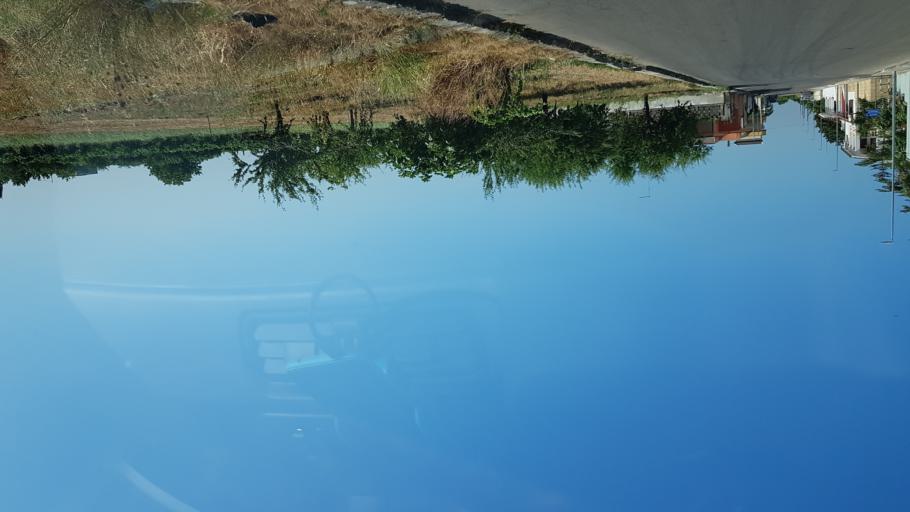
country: IT
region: Apulia
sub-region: Provincia di Brindisi
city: San Donaci
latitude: 40.4433
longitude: 17.9241
